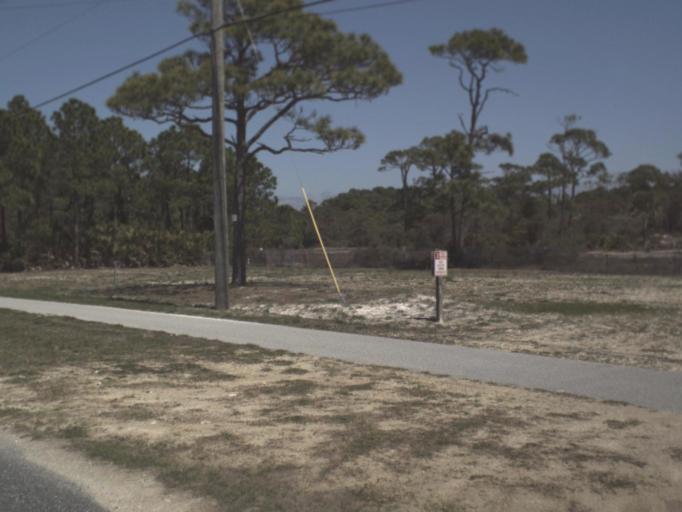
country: US
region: Florida
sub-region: Gulf County
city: Port Saint Joe
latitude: 29.7361
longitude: -85.3930
